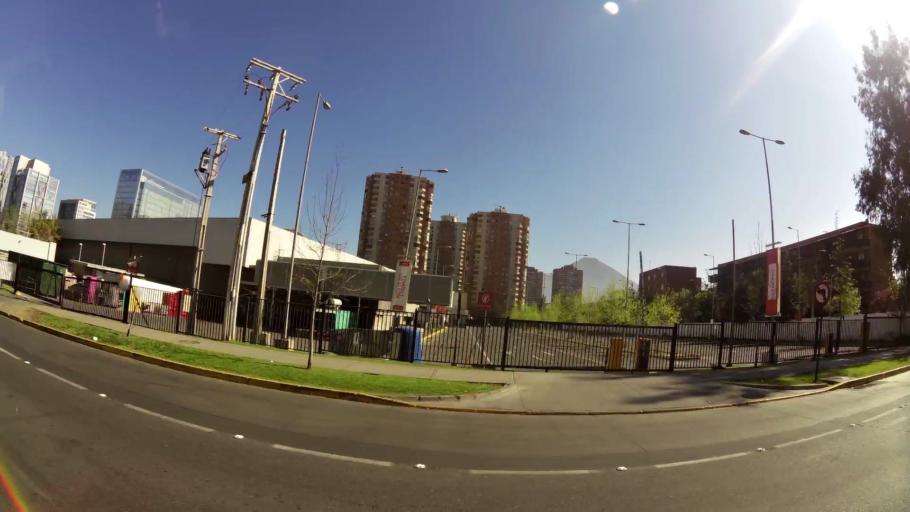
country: CL
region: Santiago Metropolitan
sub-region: Provincia de Santiago
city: Villa Presidente Frei, Nunoa, Santiago, Chile
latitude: -33.4047
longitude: -70.5675
